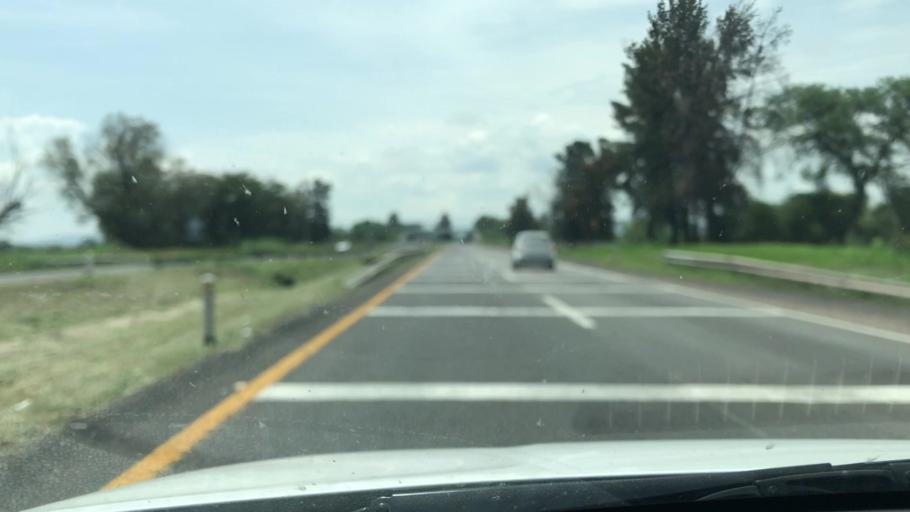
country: MX
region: Michoacan
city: Vistahermosa de Negrete
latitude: 20.2879
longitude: -102.4670
